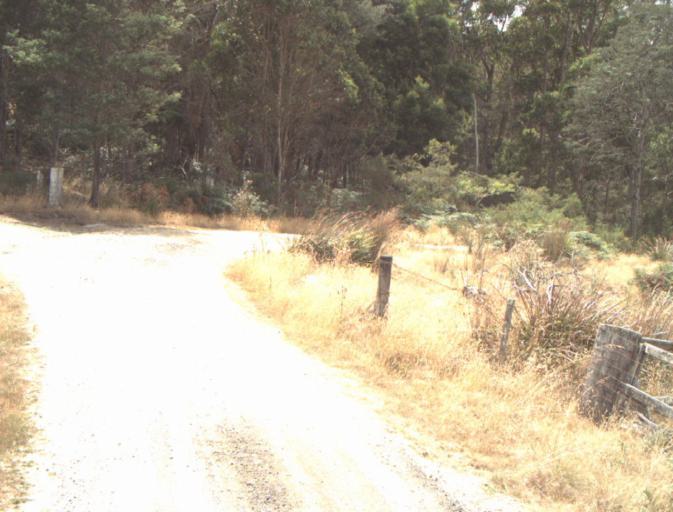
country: AU
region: Tasmania
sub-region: Launceston
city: Mayfield
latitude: -41.2079
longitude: 147.1553
